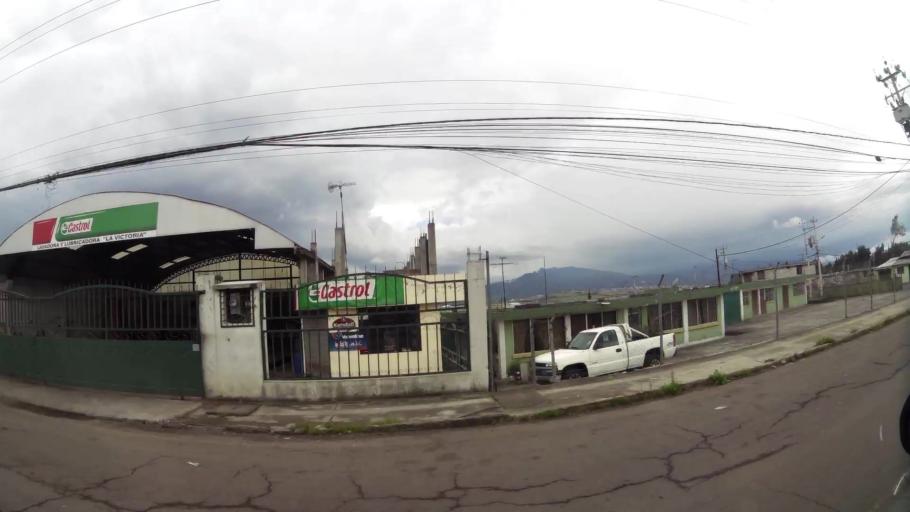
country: EC
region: Pichincha
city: Sangolqui
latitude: -0.3510
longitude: -78.5574
